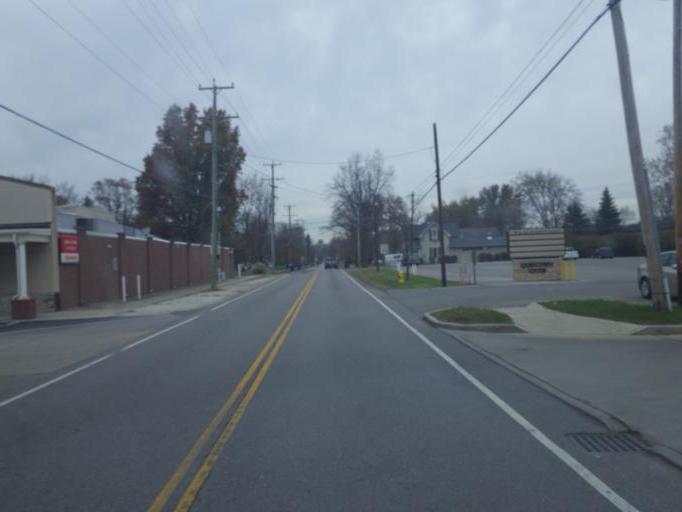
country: US
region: Ohio
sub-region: Delaware County
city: Delaware
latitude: 40.3067
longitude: -83.0903
